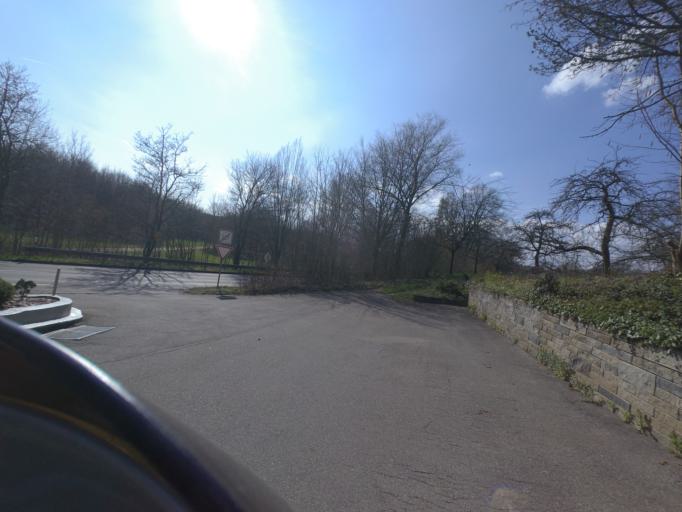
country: DE
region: Baden-Wuerttemberg
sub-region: Regierungsbezirk Stuttgart
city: Nurtingen
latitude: 48.6416
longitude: 9.3370
